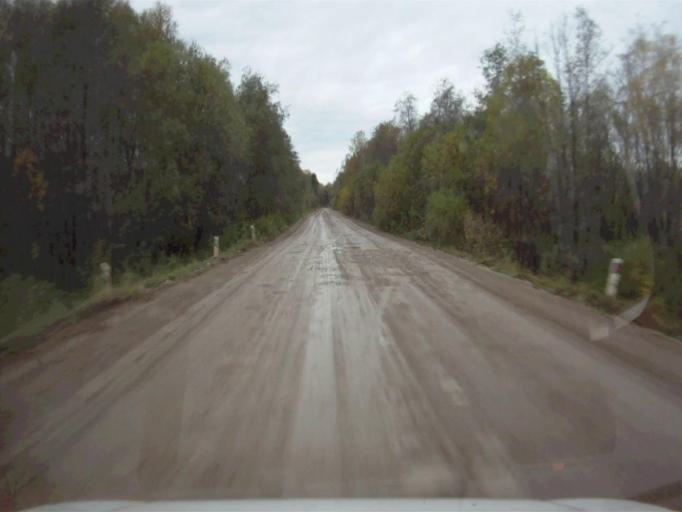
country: RU
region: Chelyabinsk
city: Nyazepetrovsk
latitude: 56.1262
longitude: 59.3449
